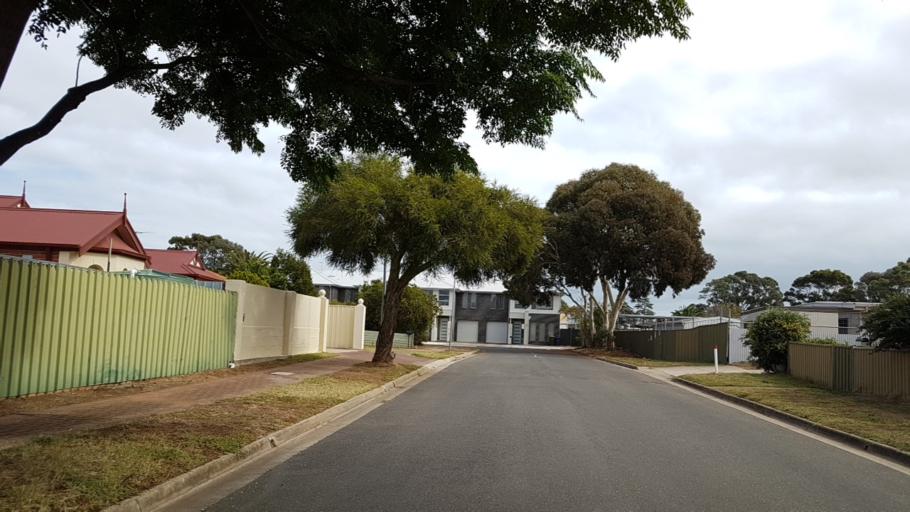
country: AU
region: South Australia
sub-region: Charles Sturt
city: Seaton
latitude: -34.9079
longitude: 138.5203
